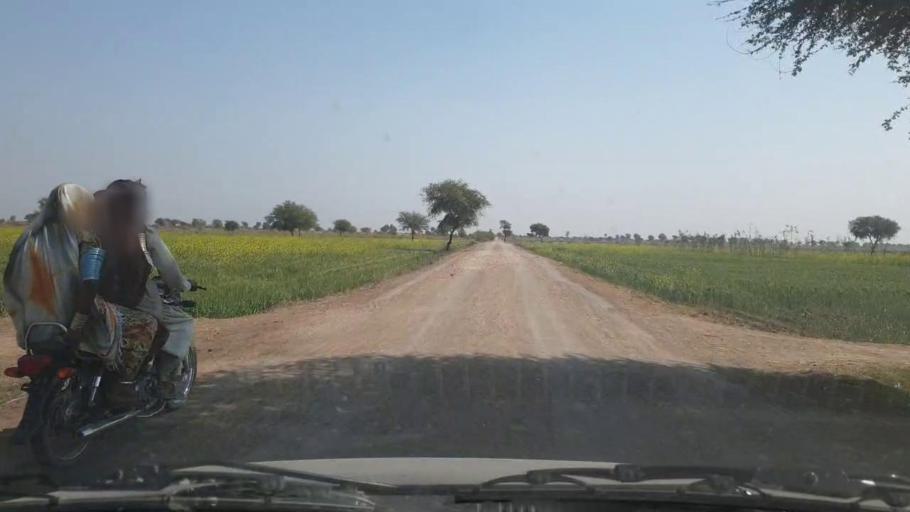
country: PK
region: Sindh
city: Samaro
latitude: 25.2432
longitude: 69.3680
